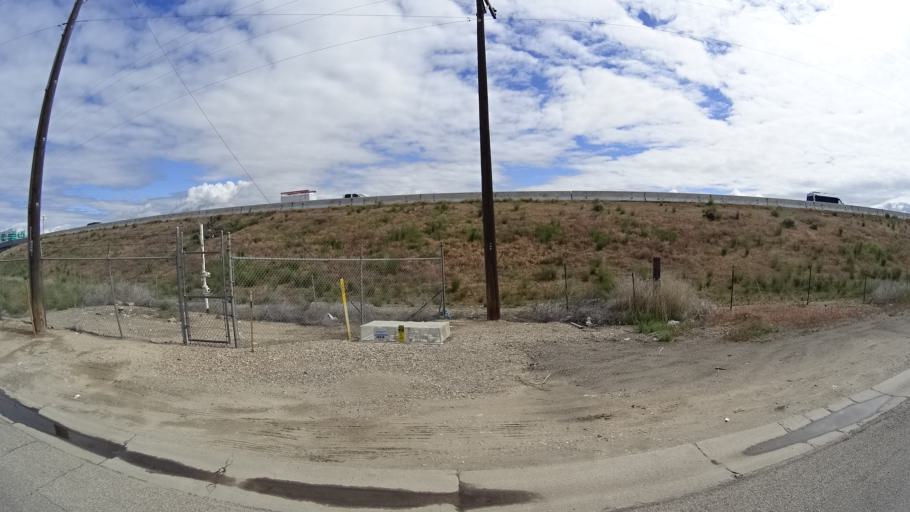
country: US
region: Idaho
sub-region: Ada County
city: Boise
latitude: 43.5626
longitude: -116.1903
